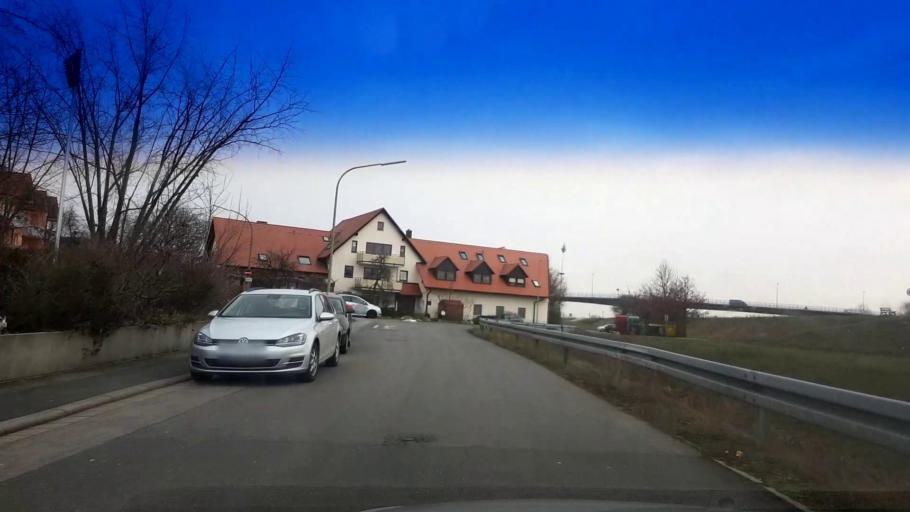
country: DE
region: Bavaria
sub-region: Upper Franconia
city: Hirschaid
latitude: 49.8164
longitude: 10.9842
